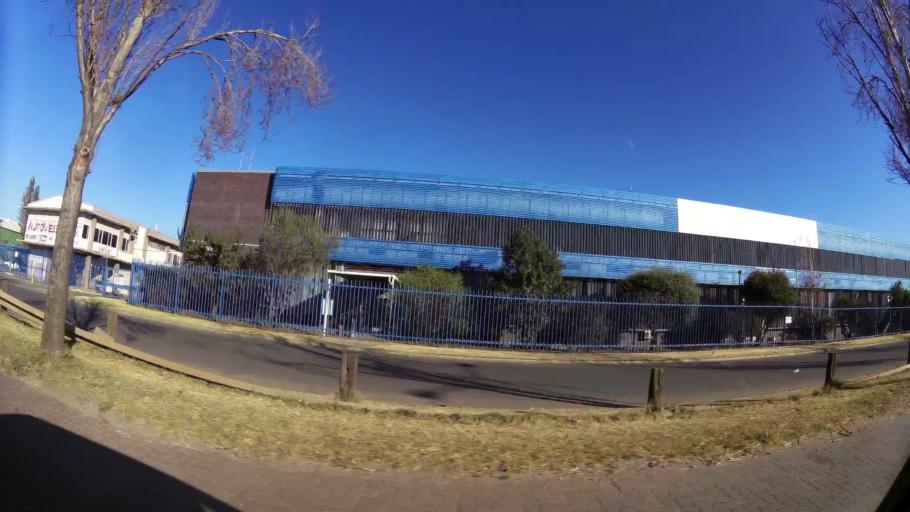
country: ZA
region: Gauteng
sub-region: Ekurhuleni Metropolitan Municipality
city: Germiston
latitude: -26.2940
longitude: 28.1377
